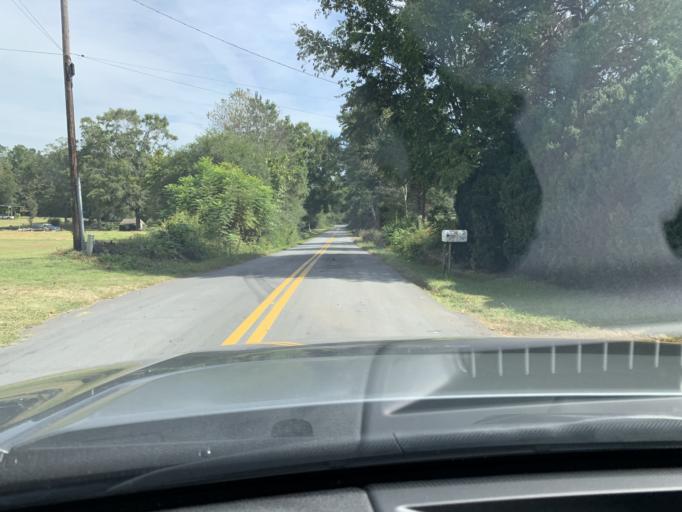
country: US
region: Georgia
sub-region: Polk County
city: Cedartown
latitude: 33.9476
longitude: -85.3691
